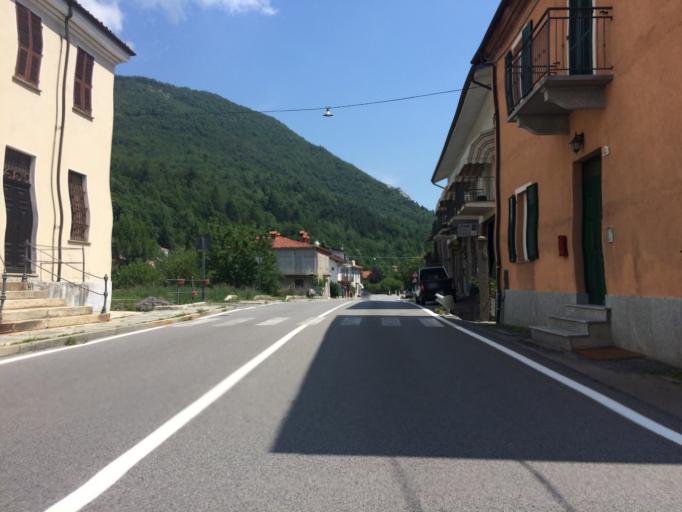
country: IT
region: Piedmont
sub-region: Provincia di Cuneo
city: Garessio
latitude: 44.1857
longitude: 7.9939
